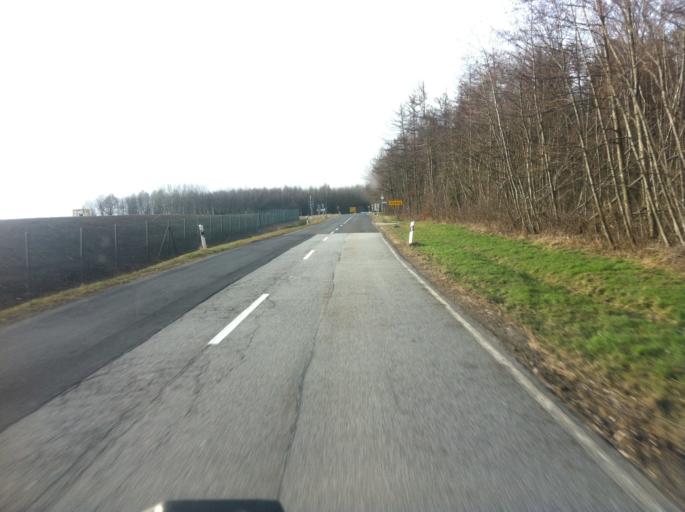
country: DE
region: Rheinland-Pfalz
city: Barenbach
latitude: 49.9620
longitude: 7.2898
